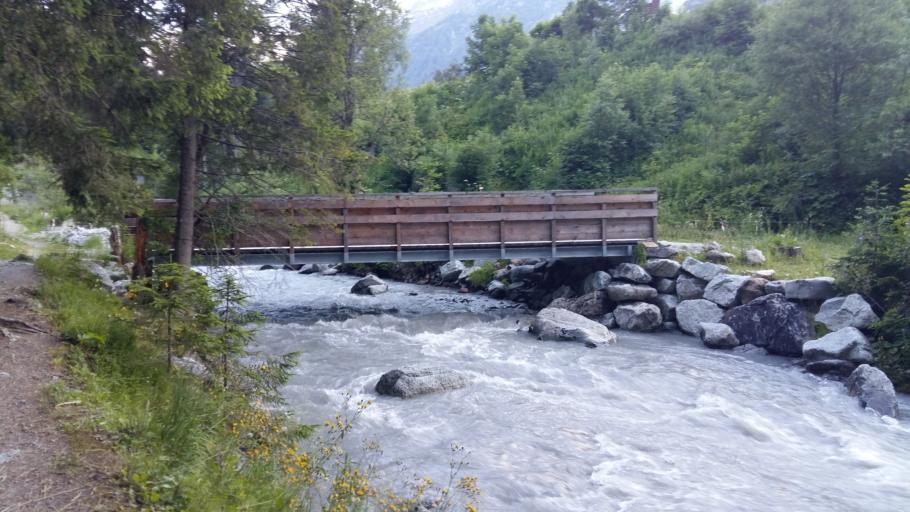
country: FR
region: Rhone-Alpes
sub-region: Departement de la Haute-Savoie
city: Chamonix-Mont-Blanc
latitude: 46.0282
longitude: 6.9276
